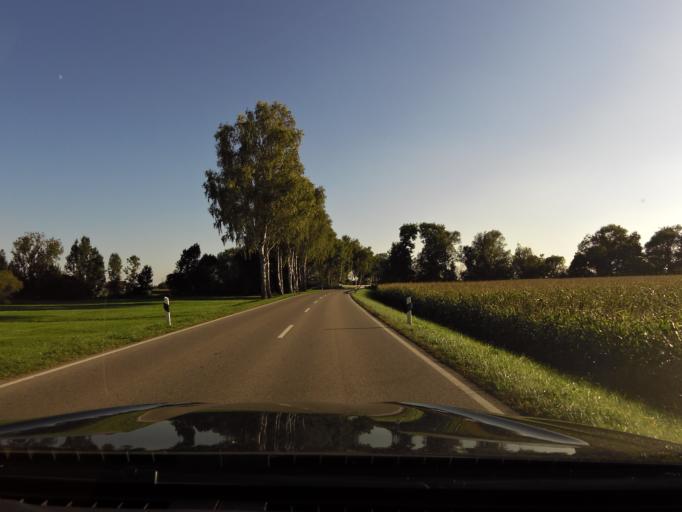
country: DE
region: Bavaria
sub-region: Upper Bavaria
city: Berglern
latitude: 48.4186
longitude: 11.9343
